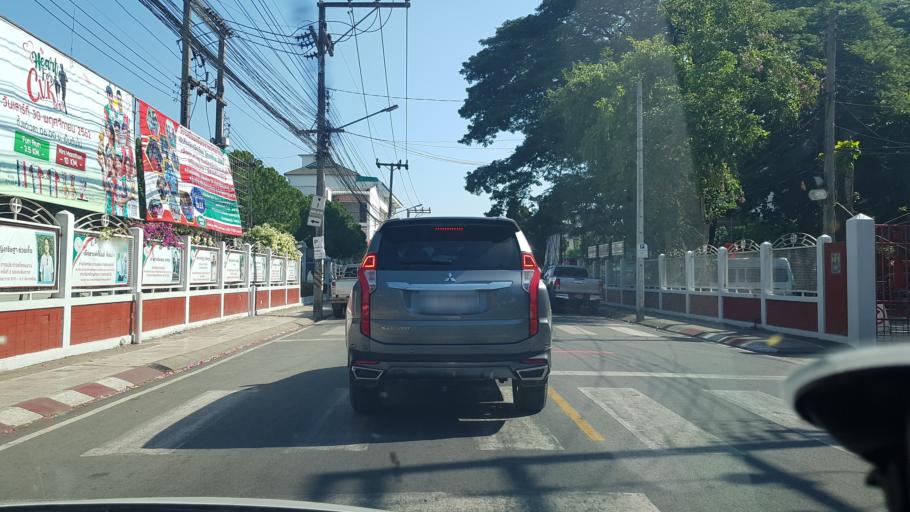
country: TH
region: Chiang Rai
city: Chiang Rai
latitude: 19.9096
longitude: 99.8269
